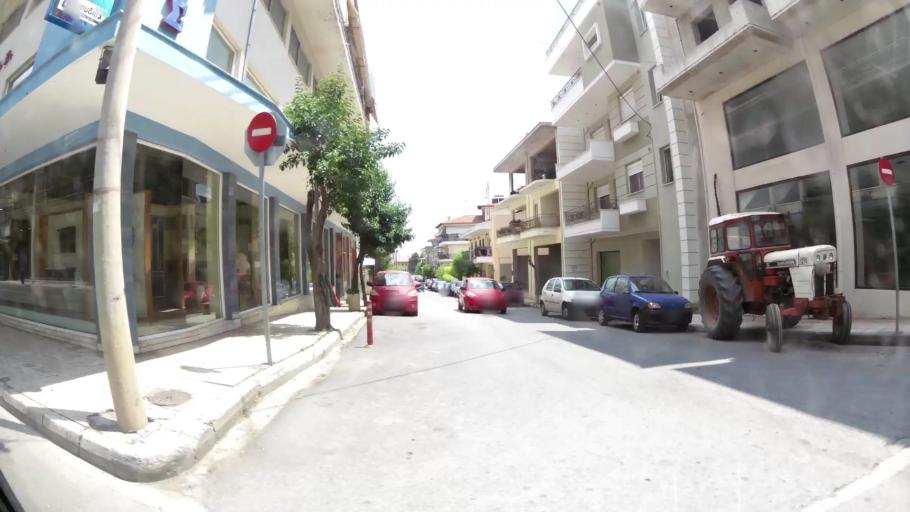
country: GR
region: West Macedonia
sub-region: Nomos Kozanis
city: Kozani
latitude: 40.2965
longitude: 21.7905
